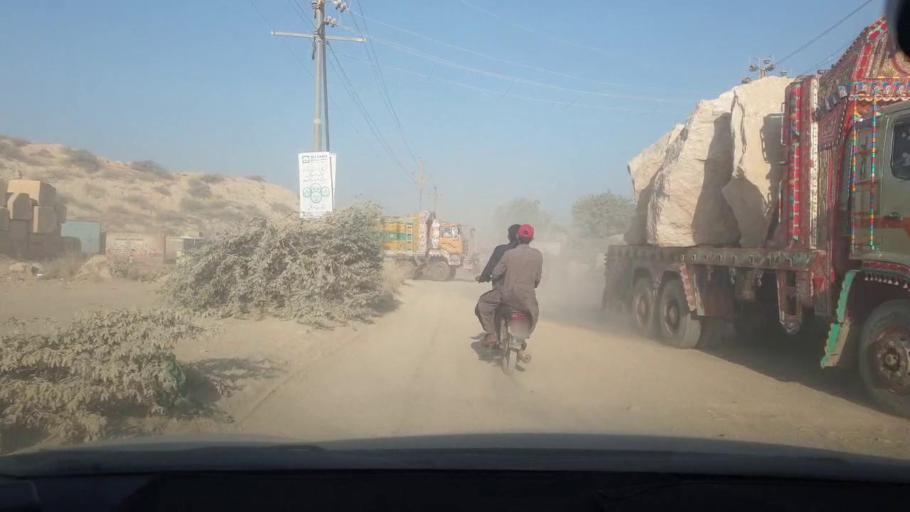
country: PK
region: Sindh
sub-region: Karachi District
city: Karachi
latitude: 24.9760
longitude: 67.0391
